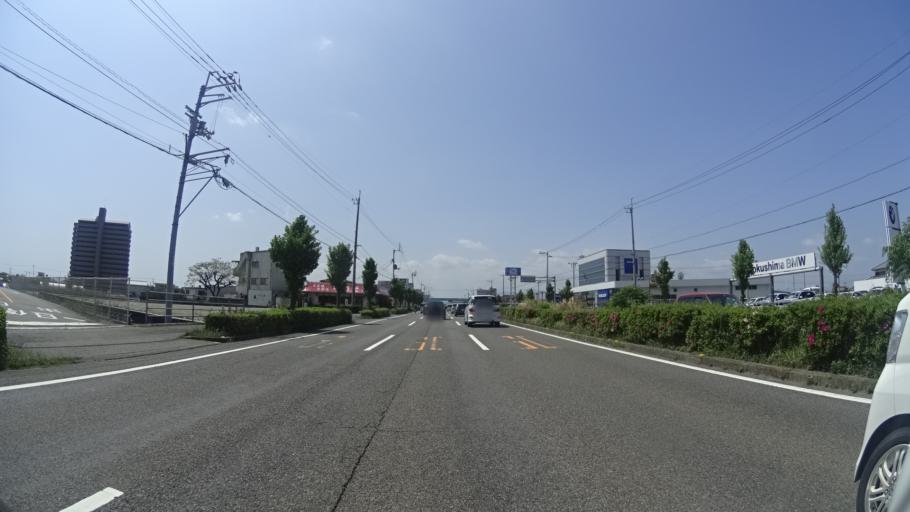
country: JP
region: Tokushima
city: Tokushima-shi
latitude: 34.1148
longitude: 134.5778
